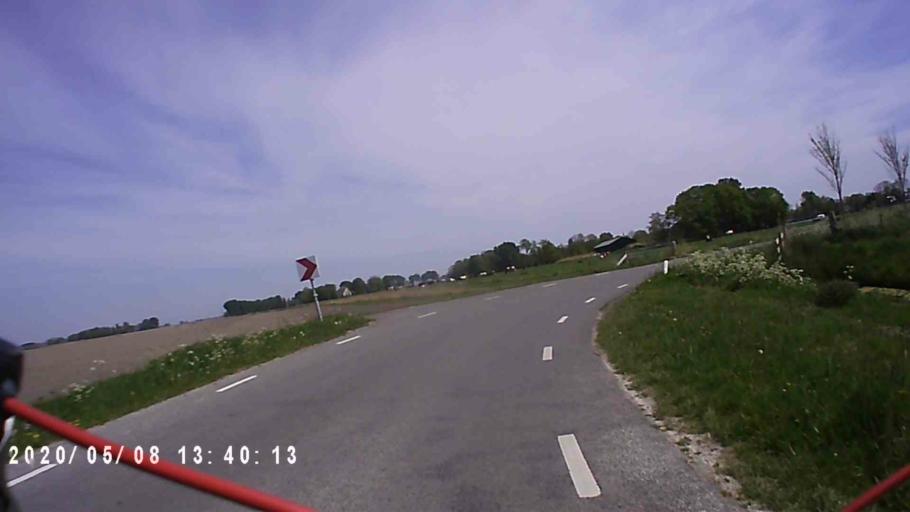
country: NL
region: Groningen
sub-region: Gemeente Appingedam
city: Appingedam
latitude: 53.3236
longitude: 6.7748
